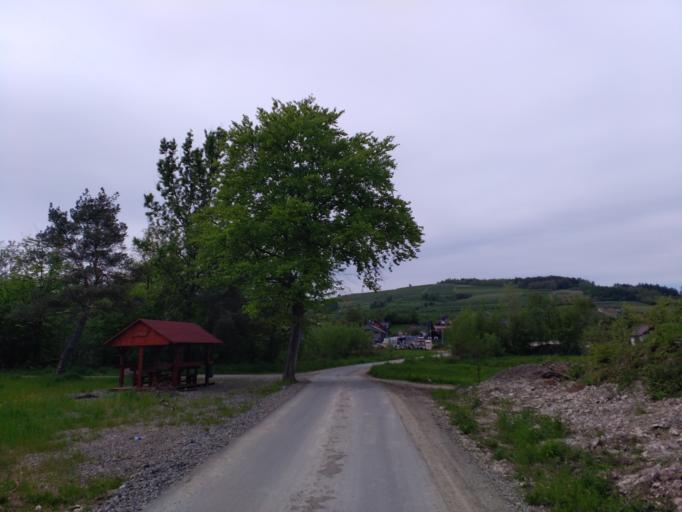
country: PL
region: Lesser Poland Voivodeship
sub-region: Powiat nowosadecki
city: Lacko
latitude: 49.5512
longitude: 20.4302
